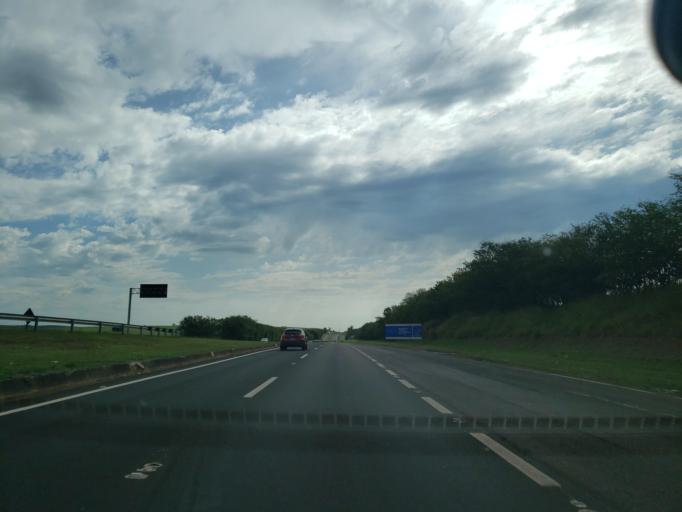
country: BR
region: Sao Paulo
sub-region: Cafelandia
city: Cafelandia
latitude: -21.8047
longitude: -49.6347
